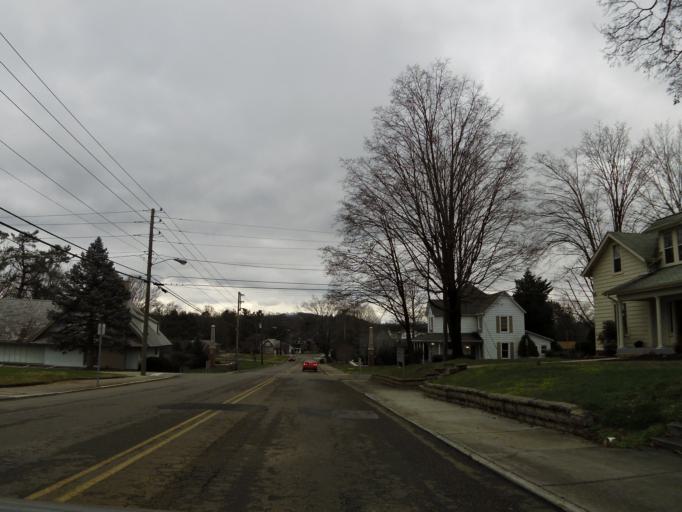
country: US
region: Tennessee
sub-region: Jefferson County
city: Jefferson City
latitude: 36.1203
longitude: -83.4924
